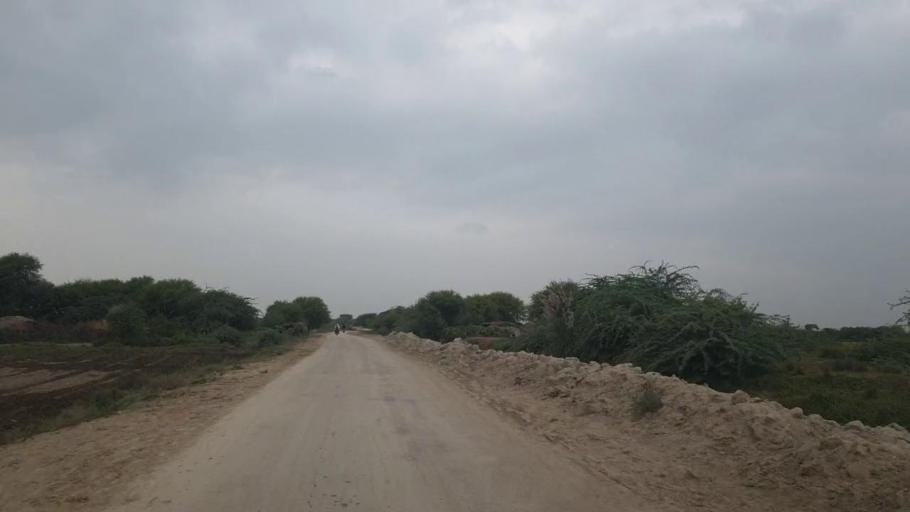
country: PK
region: Sindh
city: Badin
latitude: 24.6452
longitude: 68.6807
